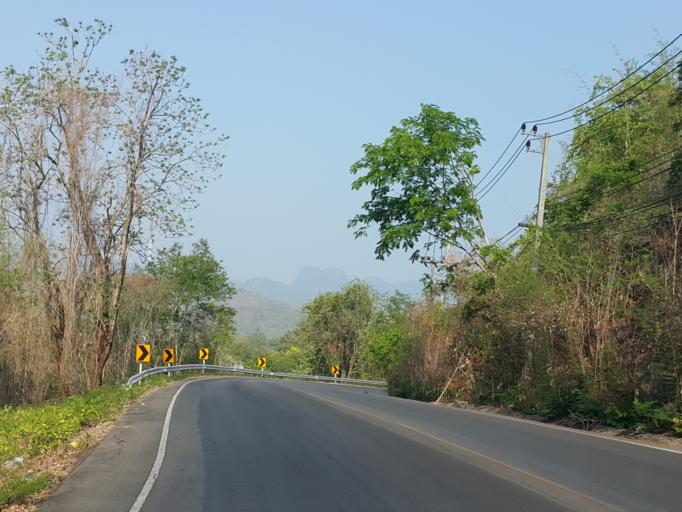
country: TH
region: Kanchanaburi
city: Sai Yok
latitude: 14.1185
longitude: 99.1481
